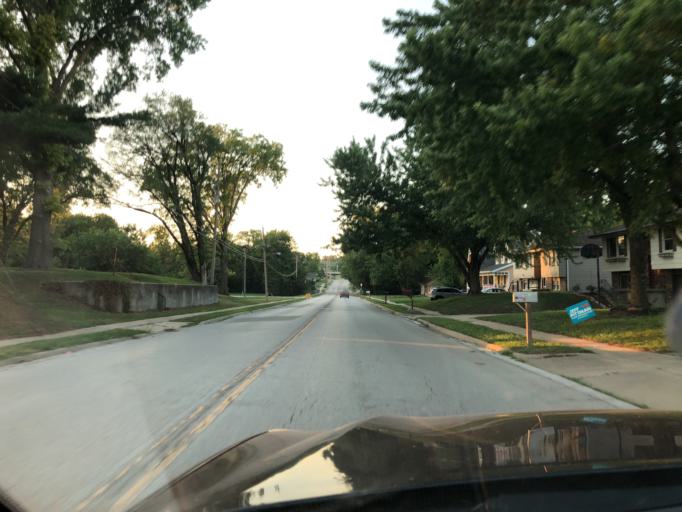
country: US
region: Kansas
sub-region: Leavenworth County
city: Leavenworth
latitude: 39.3229
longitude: -94.9506
